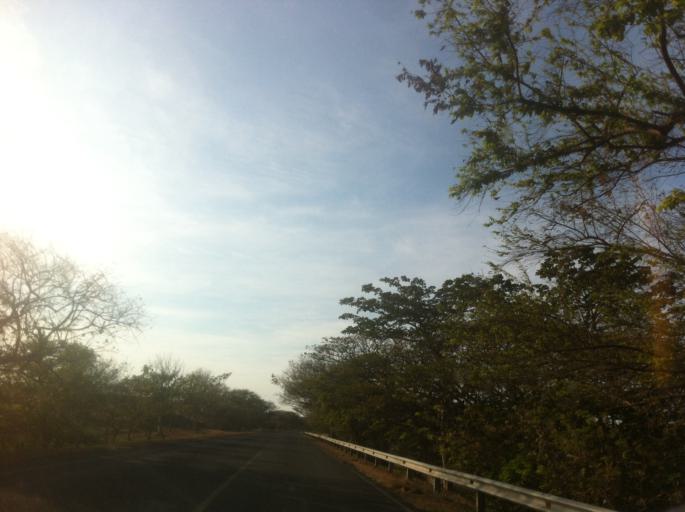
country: NI
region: Rivas
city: Cardenas
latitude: 11.2899
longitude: -85.6795
